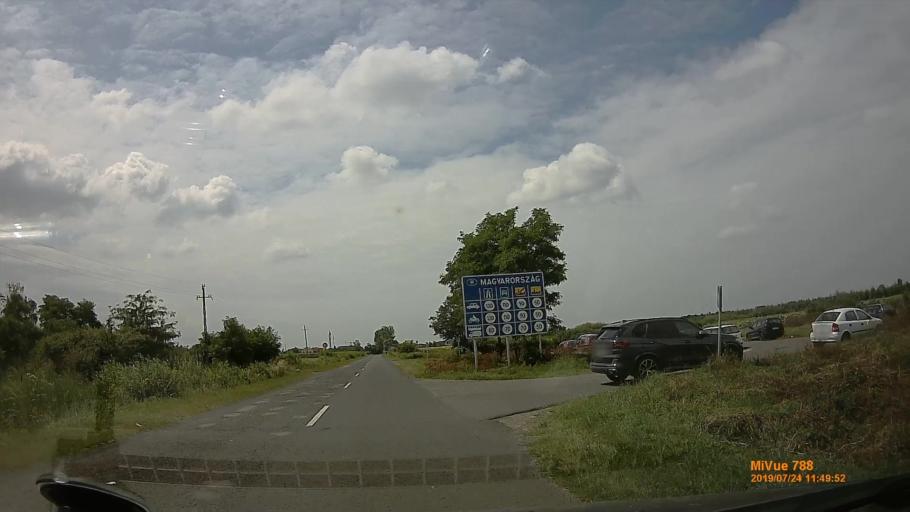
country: UA
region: Zakarpattia
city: Batiovo
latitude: 48.2439
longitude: 22.4428
